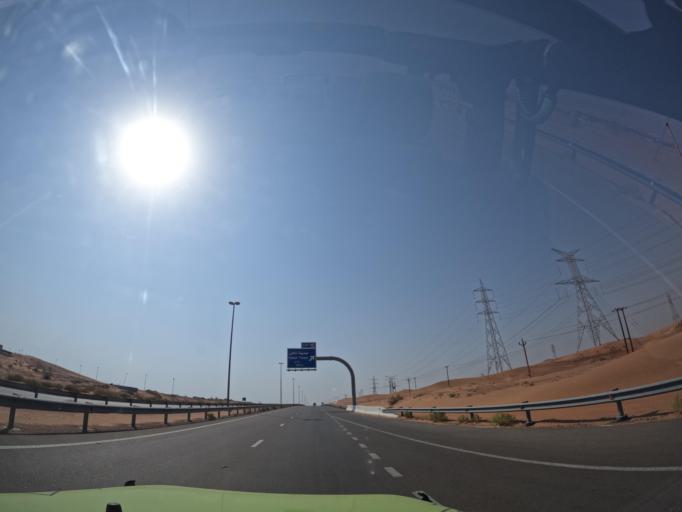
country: OM
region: Al Buraimi
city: Al Buraymi
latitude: 24.3492
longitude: 55.7376
